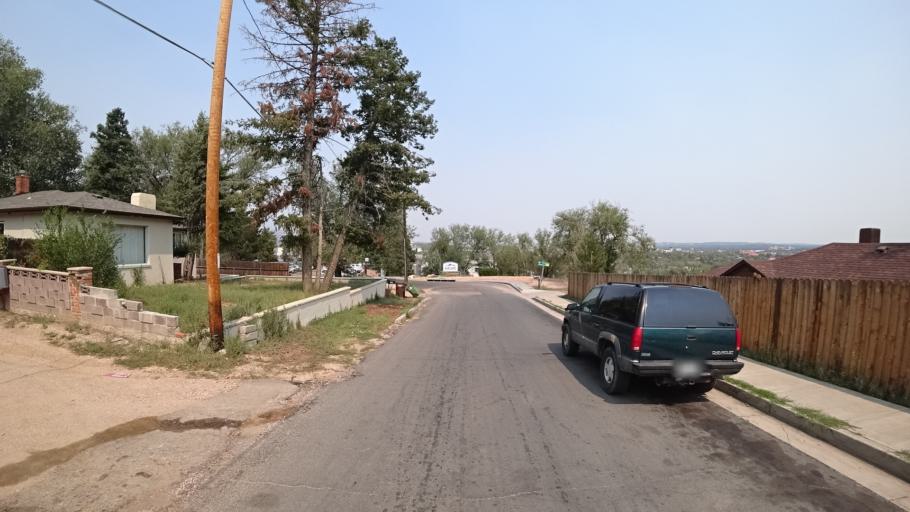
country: US
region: Colorado
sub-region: El Paso County
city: Colorado Springs
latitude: 38.8135
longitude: -104.8331
